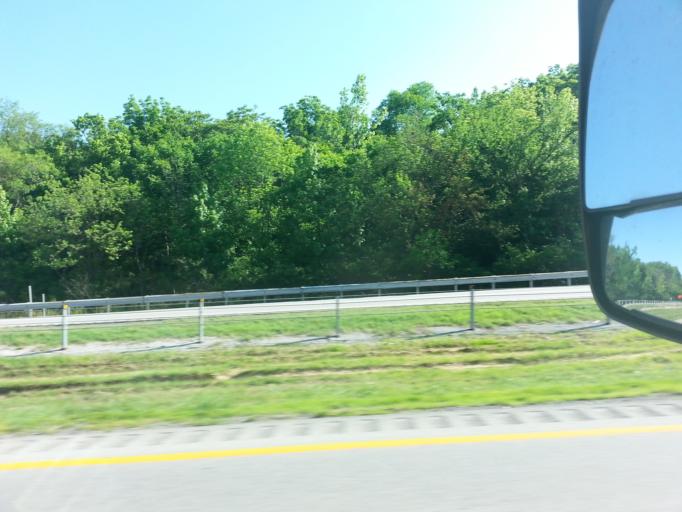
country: US
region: Indiana
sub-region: Clark County
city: Jeffersonville
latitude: 38.2507
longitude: -85.7146
